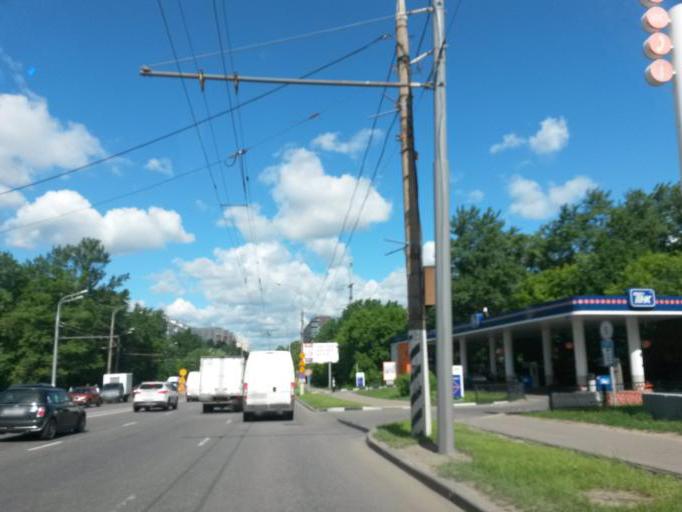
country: RU
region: Moscow
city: Kotlovka
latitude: 55.6659
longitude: 37.5983
